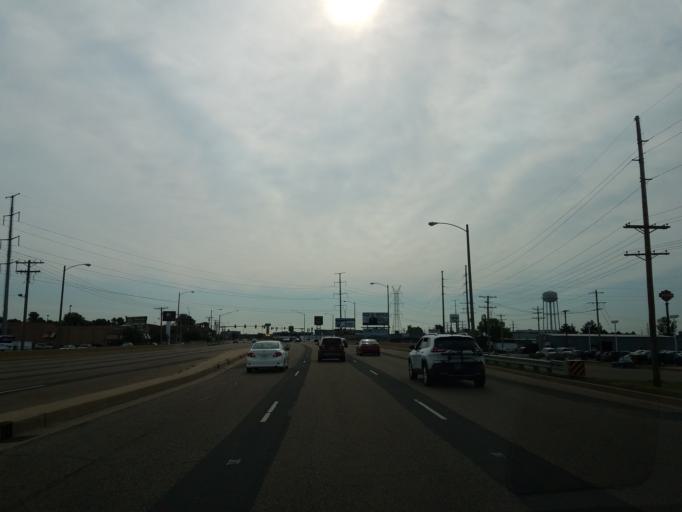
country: US
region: Illinois
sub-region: McLean County
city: Bloomington
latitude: 40.4597
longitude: -88.9692
